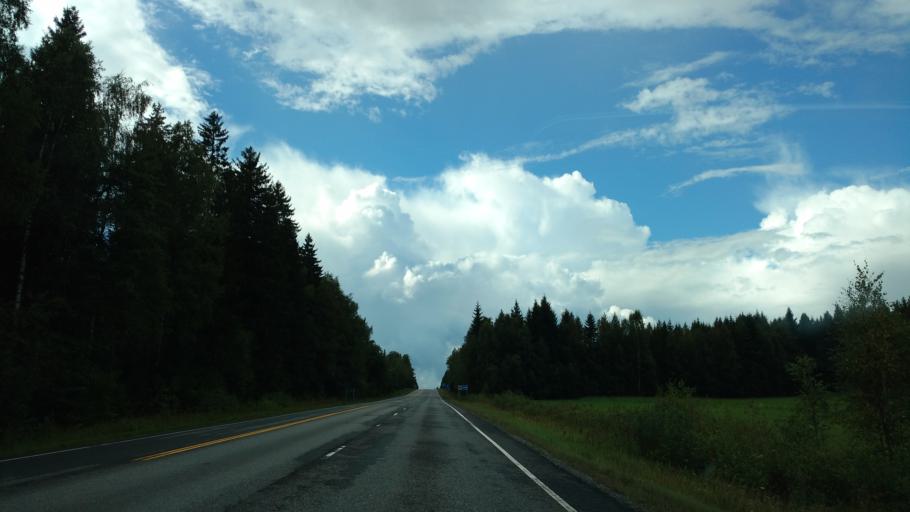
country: FI
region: Varsinais-Suomi
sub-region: Turku
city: Sauvo
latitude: 60.4001
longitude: 22.8365
